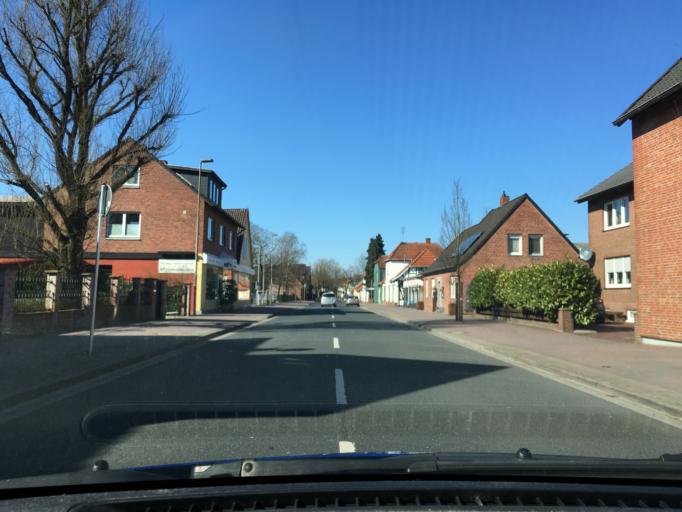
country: DE
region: Lower Saxony
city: Rotenburg
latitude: 53.1096
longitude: 9.4123
